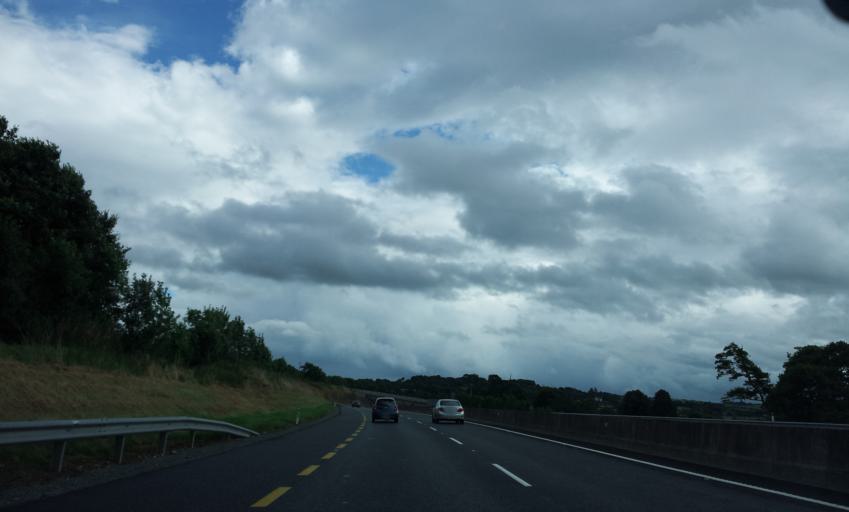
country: IE
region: Leinster
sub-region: Kilkenny
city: Mooncoin
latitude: 52.2476
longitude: -7.1907
